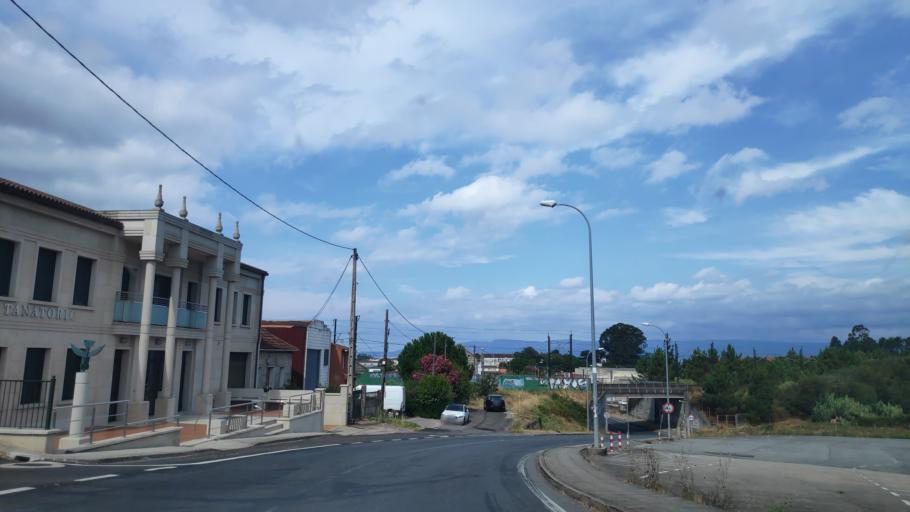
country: ES
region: Galicia
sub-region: Provincia de Pontevedra
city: Vilagarcia de Arousa
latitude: 42.5927
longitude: -8.7416
